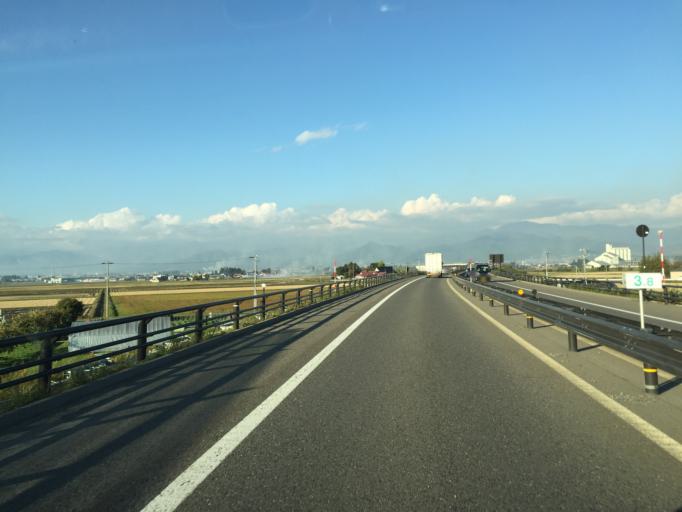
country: JP
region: Fukushima
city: Kitakata
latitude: 37.6061
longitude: 139.8775
